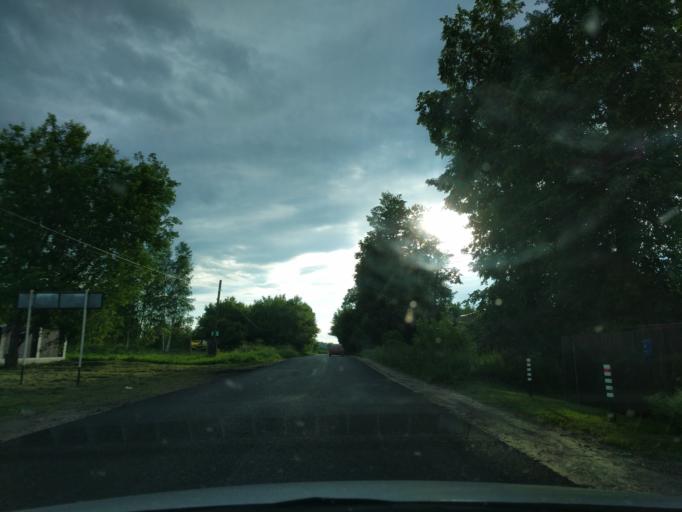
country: RU
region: Kaluga
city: Myatlevo
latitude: 54.7992
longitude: 35.7396
